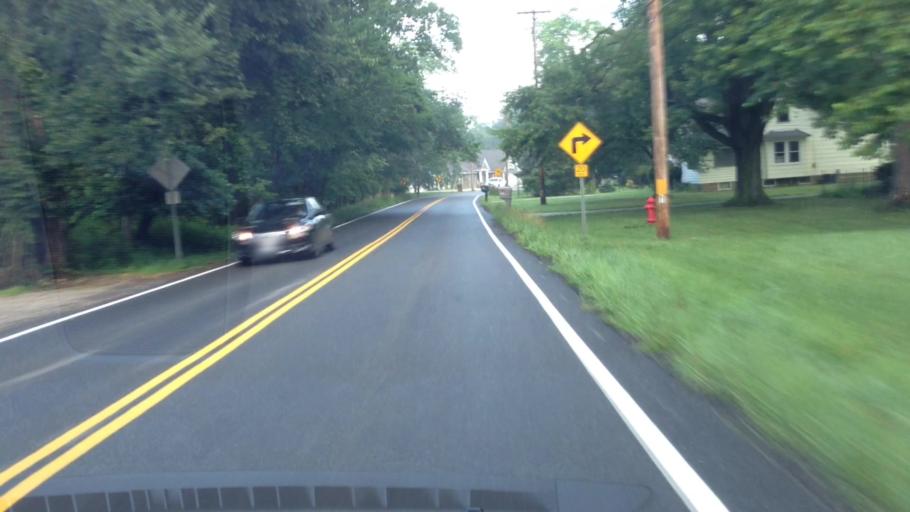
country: US
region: Ohio
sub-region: Cuyahoga County
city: Berea
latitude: 41.3580
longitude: -81.8376
